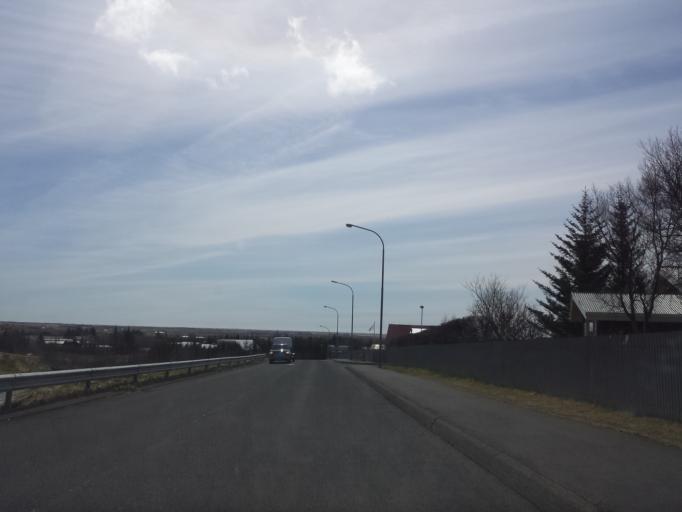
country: IS
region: South
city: Hveragerdi
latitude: 64.0037
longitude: -21.1847
